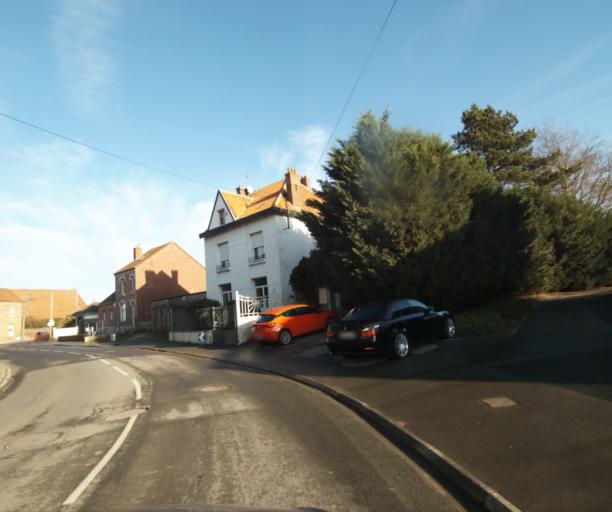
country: FR
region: Nord-Pas-de-Calais
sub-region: Departement du Nord
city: Saultain
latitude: 50.3406
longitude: 3.5783
